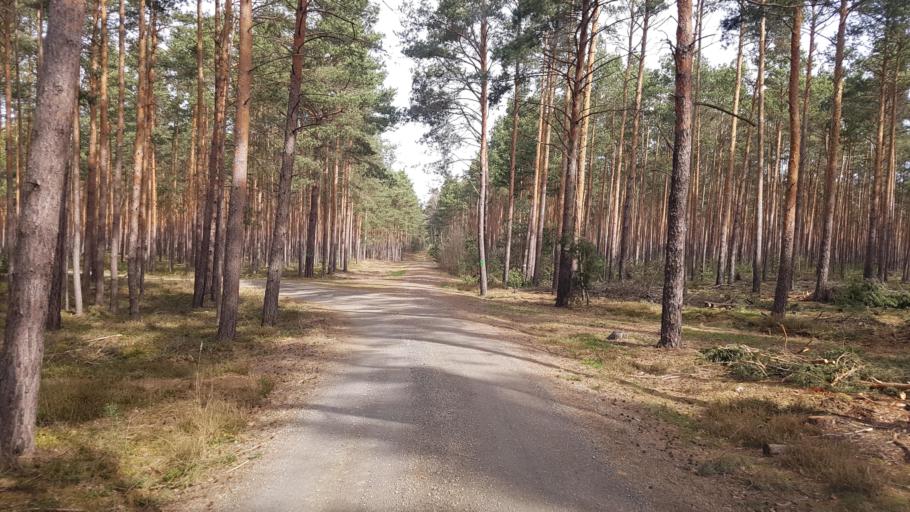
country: DE
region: Brandenburg
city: Bad Liebenwerda
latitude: 51.4949
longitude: 13.4594
